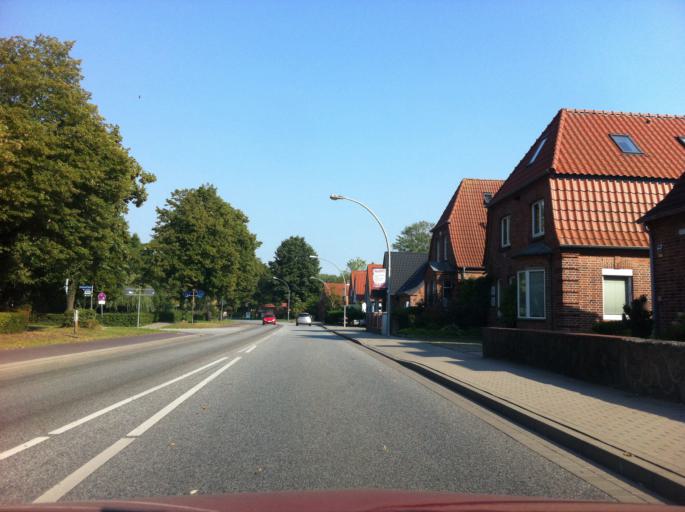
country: DE
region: Schleswig-Holstein
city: Oldenburg in Holstein
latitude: 54.2901
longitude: 10.8929
